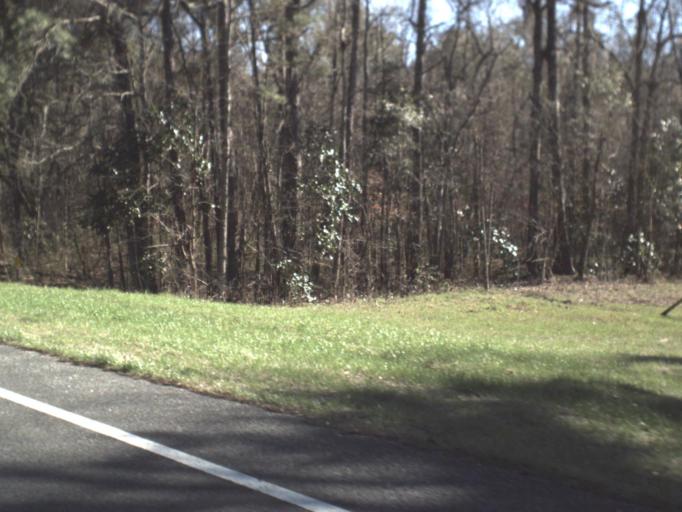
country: US
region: Florida
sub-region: Gadsden County
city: Midway
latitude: 30.5154
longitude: -84.4624
